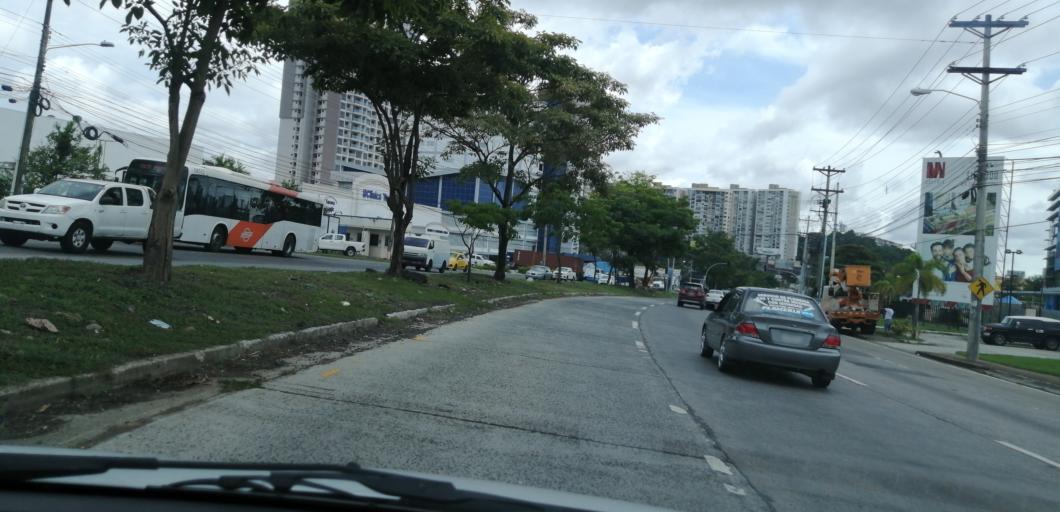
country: PA
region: Panama
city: Panama
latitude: 9.0299
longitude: -79.5178
